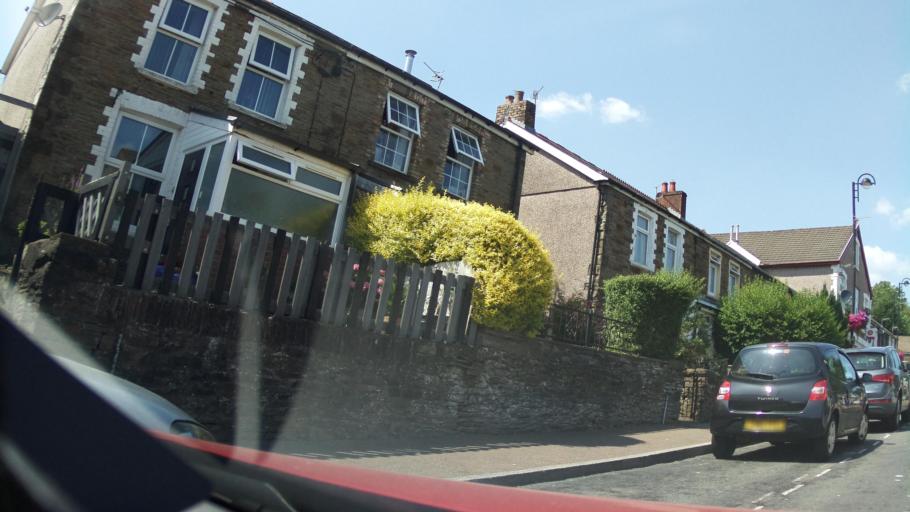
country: GB
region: Wales
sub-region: Caerphilly County Borough
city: Ystrad Mynach
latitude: 51.6420
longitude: -3.2369
